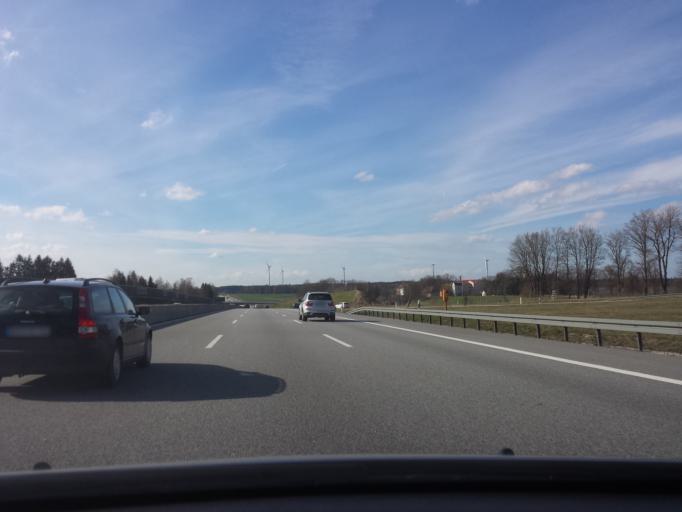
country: DE
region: Bavaria
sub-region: Upper Bavaria
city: Odelzhausen
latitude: 48.3080
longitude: 11.2071
